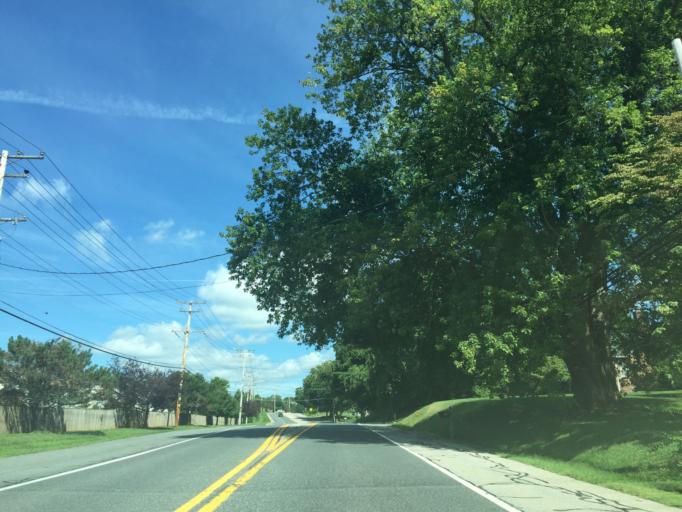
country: US
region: Maryland
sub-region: Harford County
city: North Bel Air
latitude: 39.5518
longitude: -76.3517
